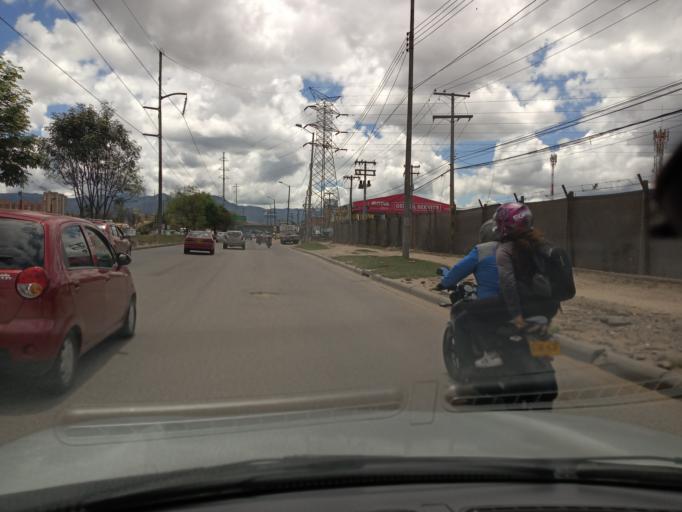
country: CO
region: Bogota D.C.
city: Bogota
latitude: 4.6620
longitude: -74.1383
